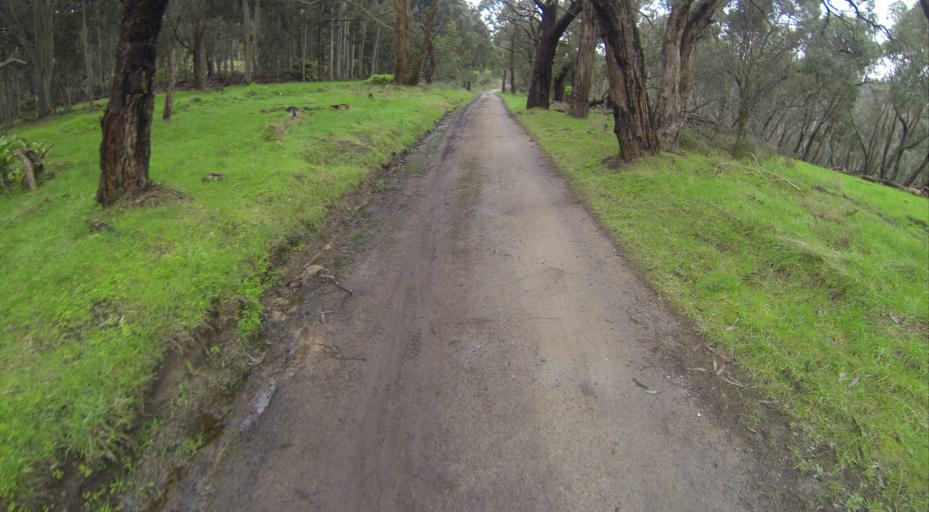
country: AU
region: Victoria
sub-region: Yarra Ranges
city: Lysterfield
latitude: -37.9361
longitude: 145.3125
